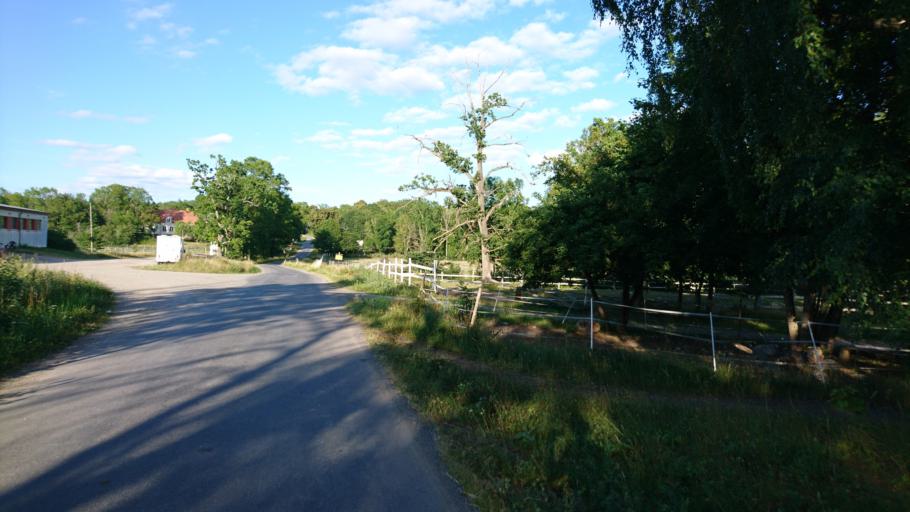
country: SE
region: Soedermanland
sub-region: Strangnas Kommun
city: Stallarholmen
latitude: 59.3843
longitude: 17.2989
